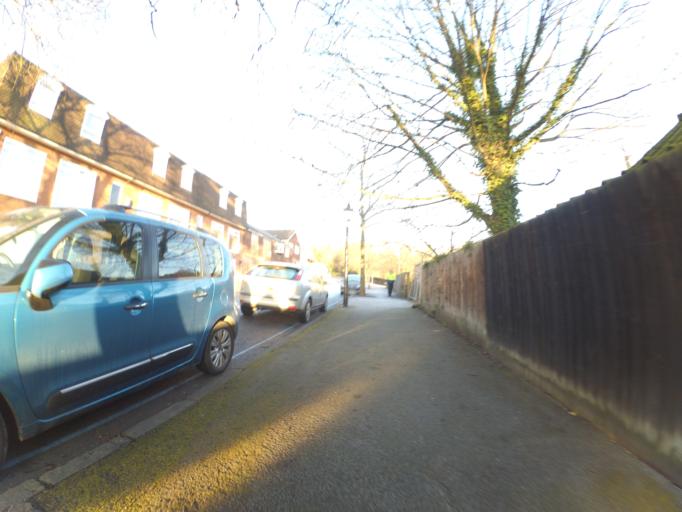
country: GB
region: England
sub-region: Nottingham
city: Nottingham
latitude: 52.9526
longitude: -1.1618
